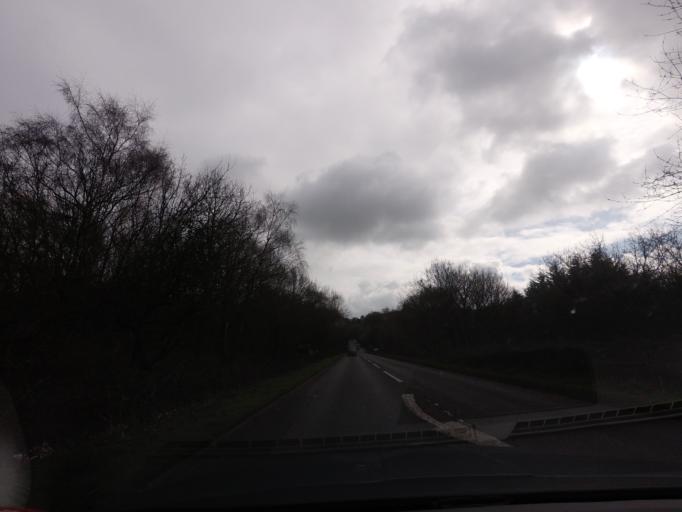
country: GB
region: England
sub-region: Kent
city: Kemsing
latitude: 51.2789
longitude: 0.2593
